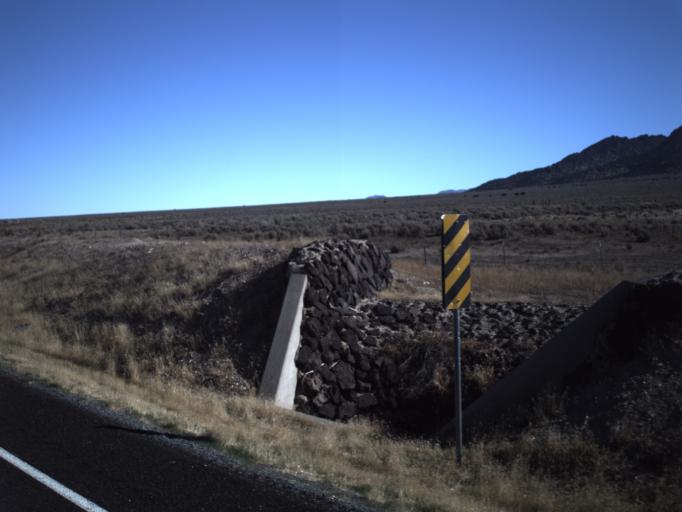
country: US
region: Utah
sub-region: Beaver County
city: Milford
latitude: 38.2949
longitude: -112.9683
